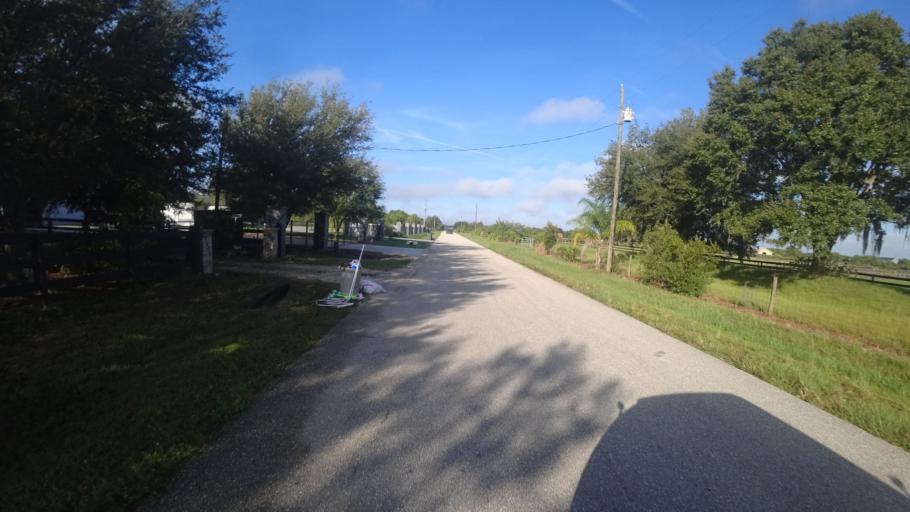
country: US
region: Florida
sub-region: Sarasota County
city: The Meadows
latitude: 27.4165
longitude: -82.3087
